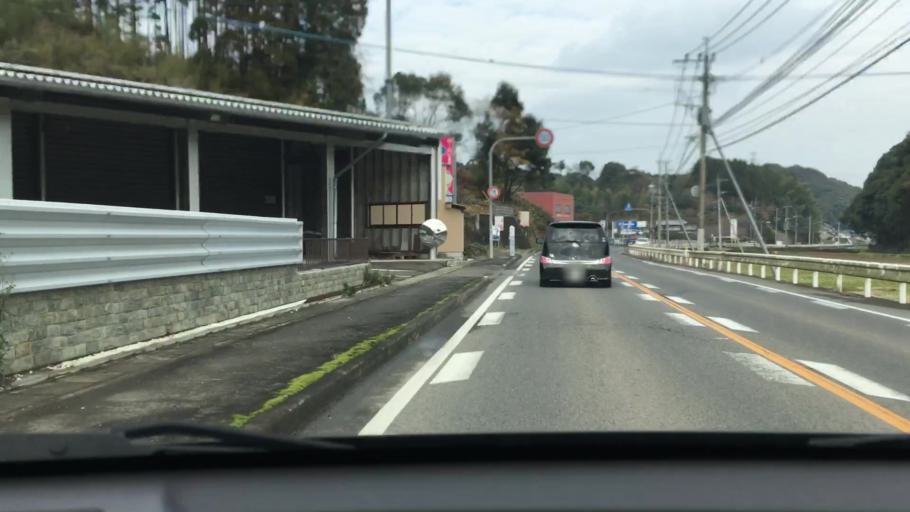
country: JP
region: Saga Prefecture
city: Imaricho-ko
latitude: 33.2995
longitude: 129.9179
